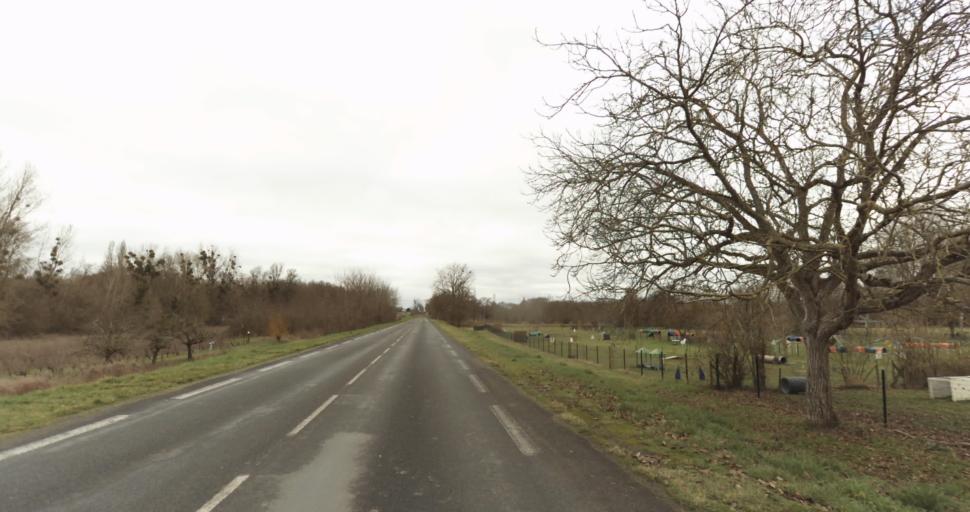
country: FR
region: Pays de la Loire
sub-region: Departement de Maine-et-Loire
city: Distre
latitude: 47.2194
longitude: -0.1130
